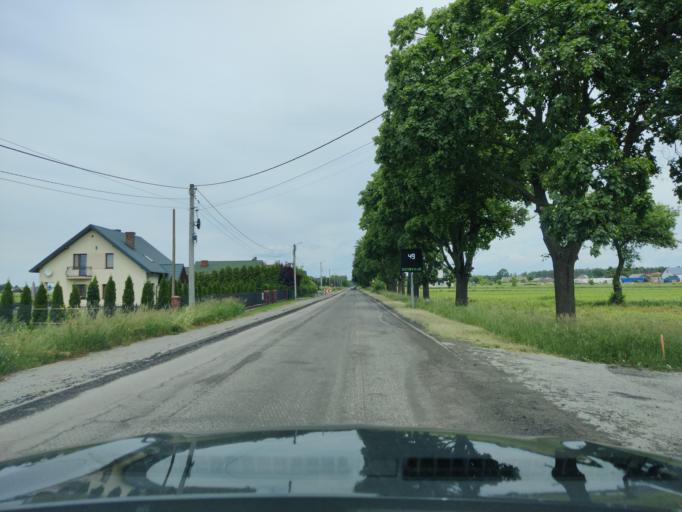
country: PL
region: Masovian Voivodeship
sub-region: Powiat wyszkowski
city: Rzasnik
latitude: 52.6911
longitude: 21.4219
